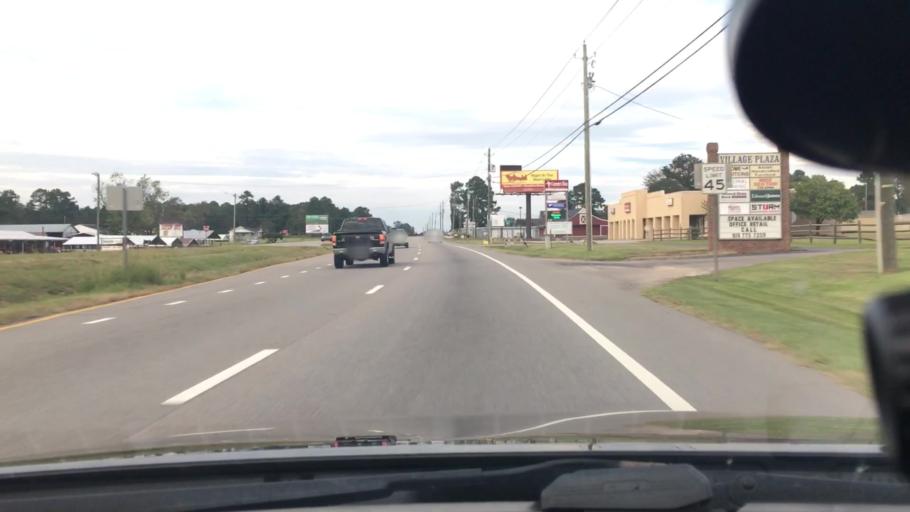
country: US
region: North Carolina
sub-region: Lee County
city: Sanford
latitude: 35.4301
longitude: -79.2215
